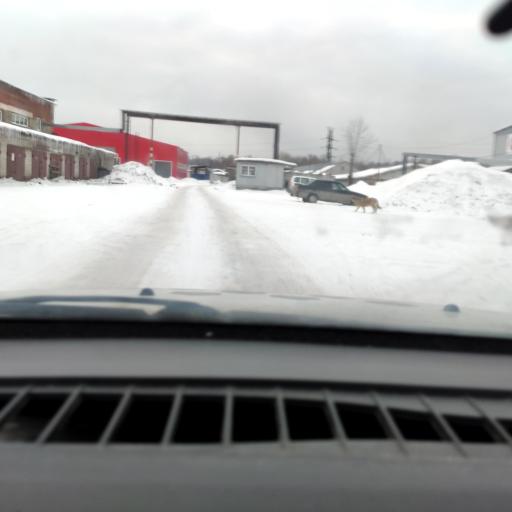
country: RU
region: Perm
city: Perm
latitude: 58.1063
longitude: 56.3483
